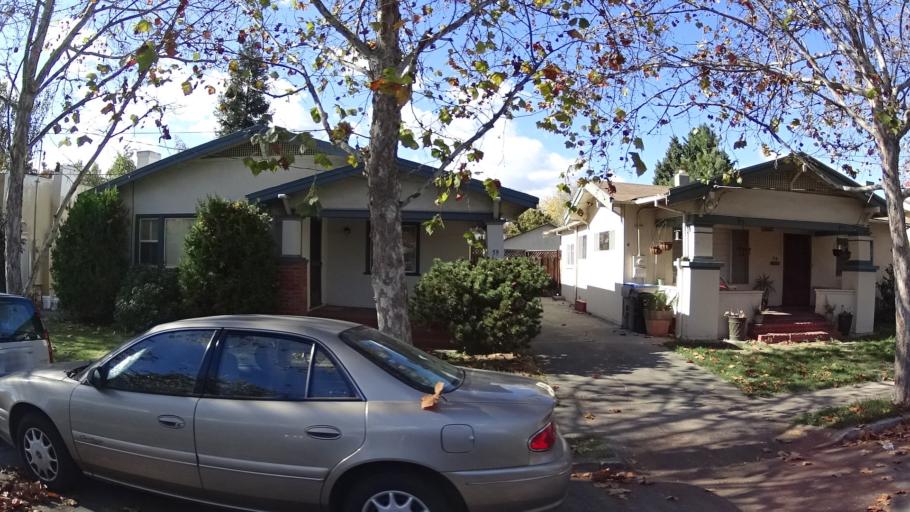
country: US
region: California
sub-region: Santa Clara County
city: Buena Vista
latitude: 37.3302
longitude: -121.9074
